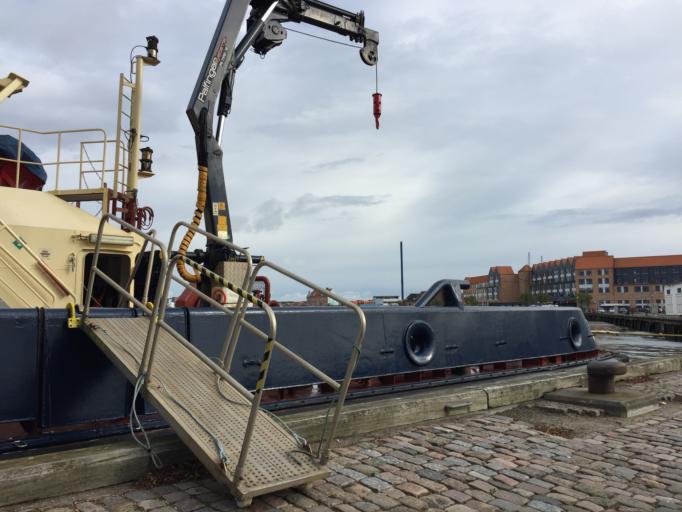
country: DK
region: Zealand
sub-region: Slagelse Kommune
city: Korsor
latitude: 55.3332
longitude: 11.1377
